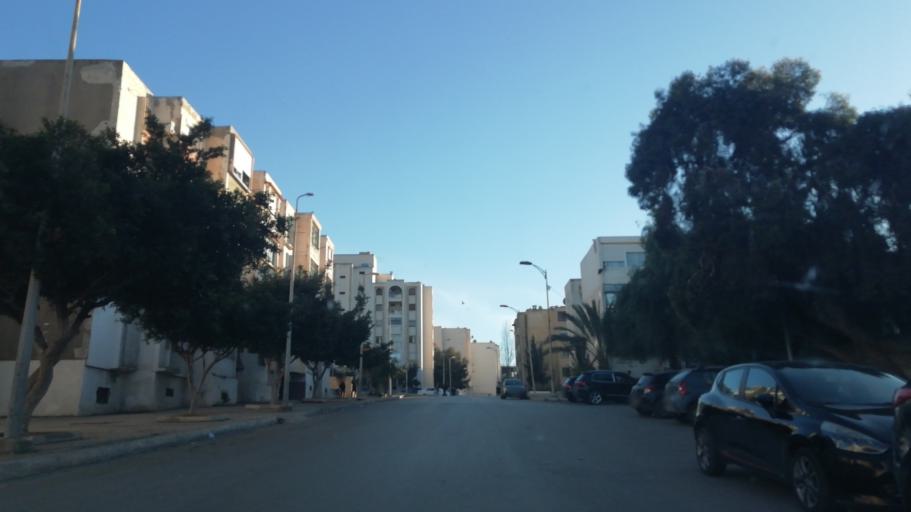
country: DZ
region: Oran
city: Oran
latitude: 35.7197
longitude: -0.5978
